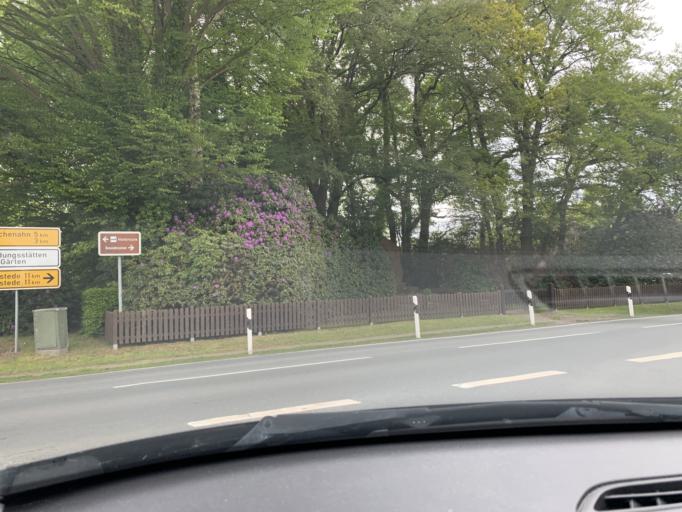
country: DE
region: Lower Saxony
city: Bad Zwischenahn
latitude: 53.2152
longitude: 8.0092
